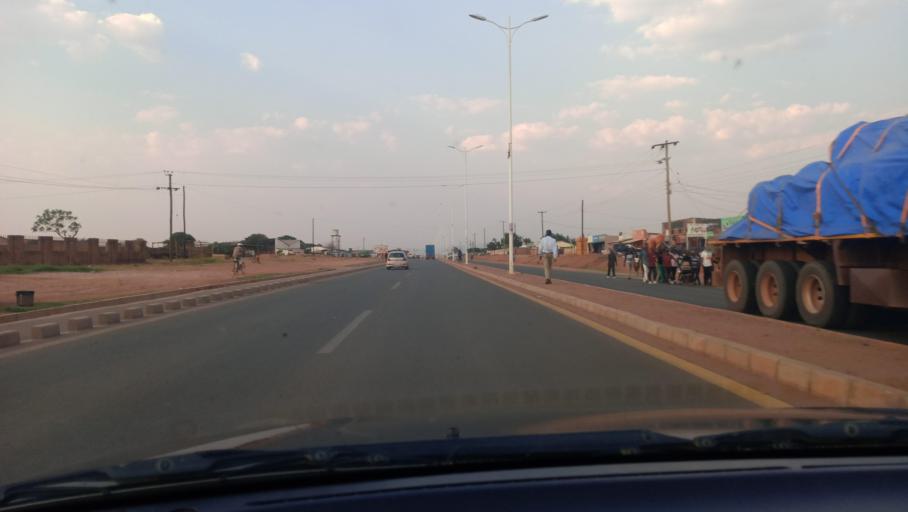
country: ZM
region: Northern
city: Mpika
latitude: -11.8418
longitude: 31.4446
